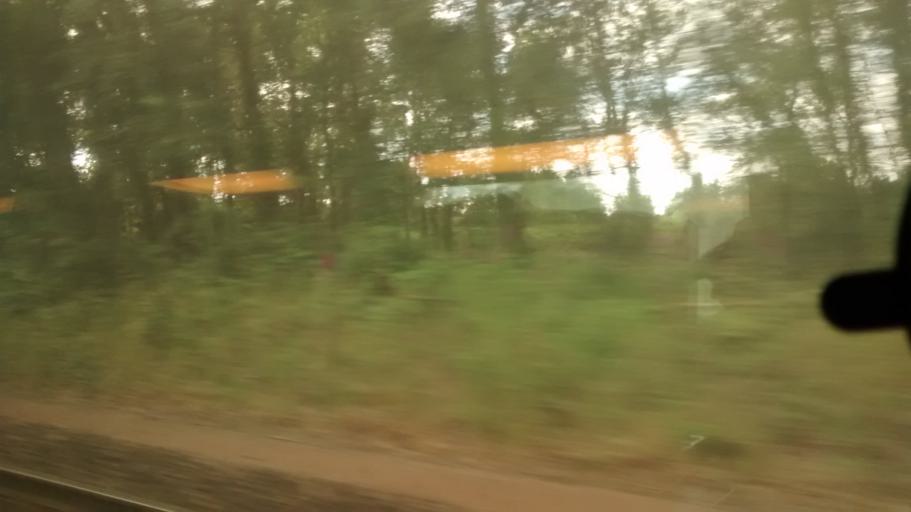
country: FR
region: Pays de la Loire
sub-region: Departement de la Sarthe
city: Change
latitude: 48.0076
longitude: 0.2845
